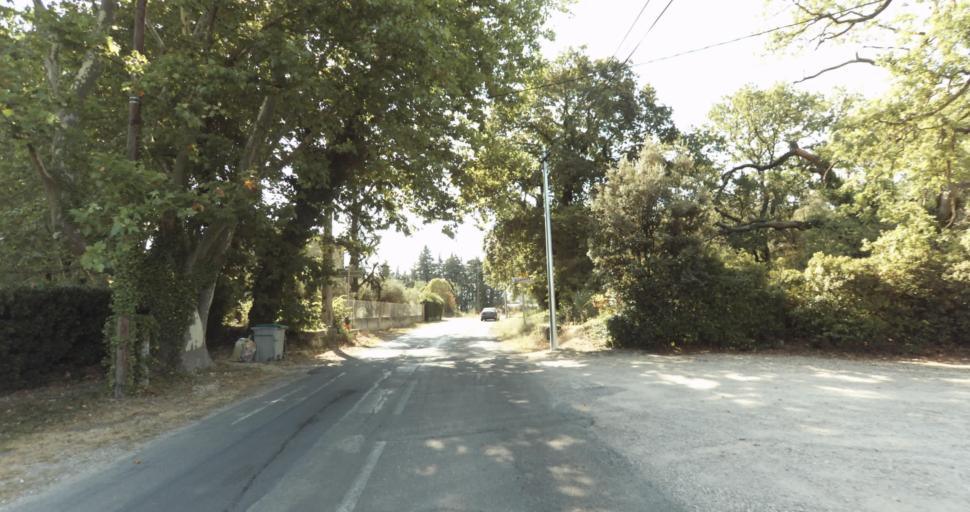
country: FR
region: Provence-Alpes-Cote d'Azur
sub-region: Departement du Vaucluse
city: Monteux
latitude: 44.0307
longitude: 5.0102
